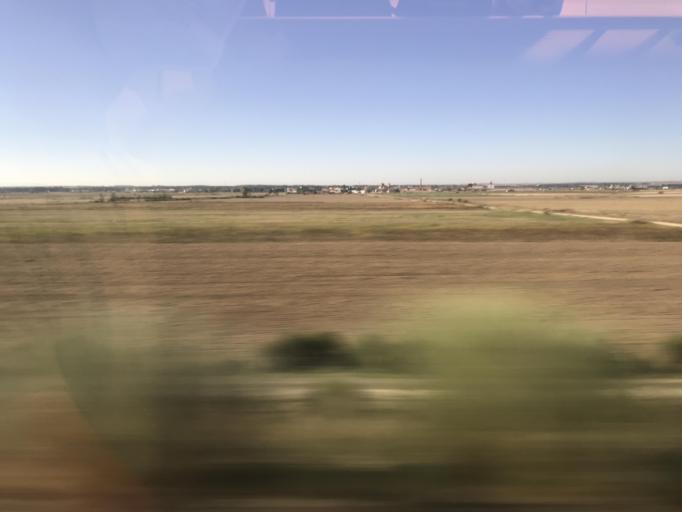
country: ES
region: Castille and Leon
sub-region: Provincia de Segovia
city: Nava de la Asuncion
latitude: 41.1696
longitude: -4.4783
